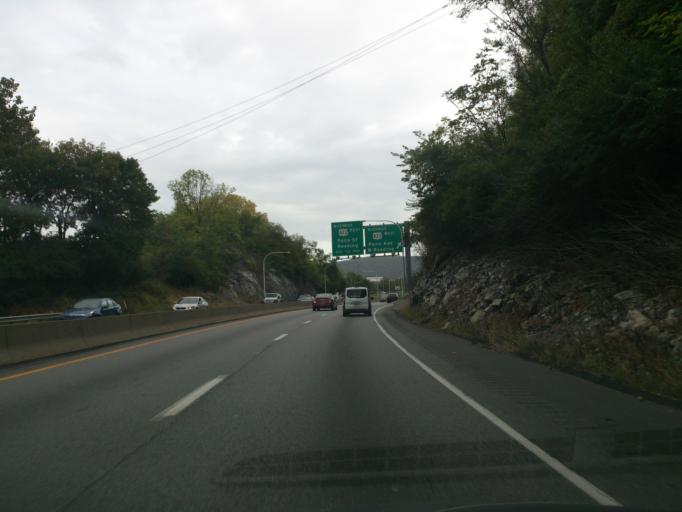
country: US
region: Pennsylvania
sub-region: Berks County
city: West Reading
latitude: 40.3380
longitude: -75.9423
